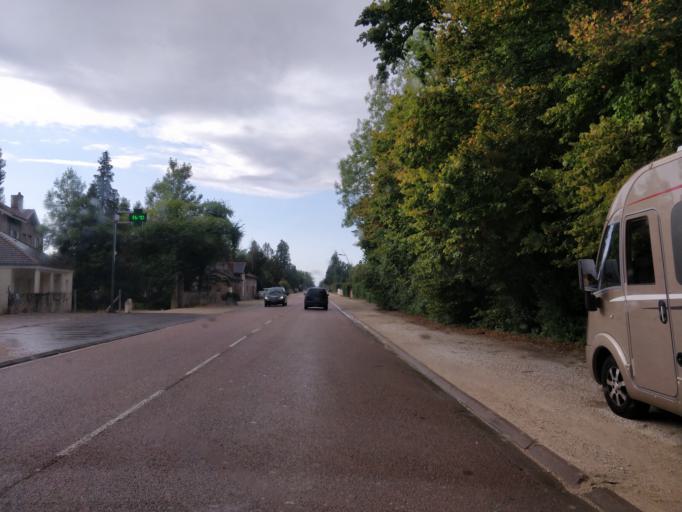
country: FR
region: Champagne-Ardenne
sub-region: Departement de l'Aube
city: Lusigny-sur-Barse
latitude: 48.2539
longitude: 4.2601
